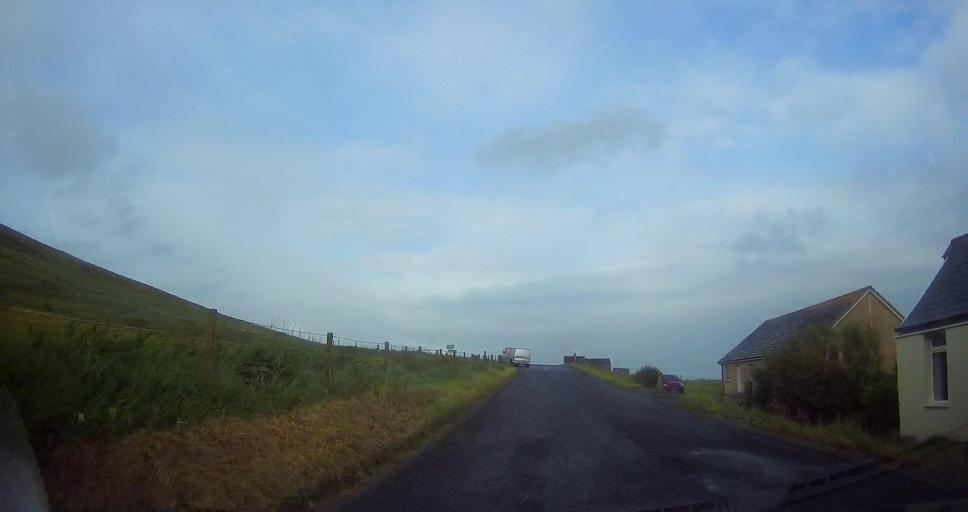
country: GB
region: Scotland
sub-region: Orkney Islands
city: Stromness
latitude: 58.9194
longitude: -3.1829
